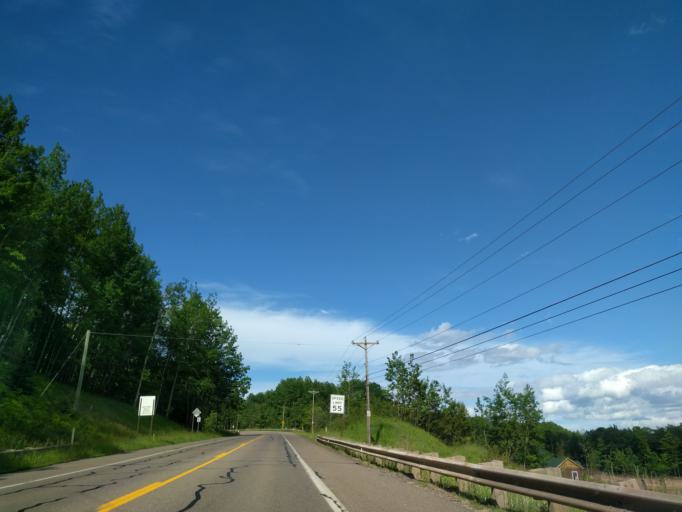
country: US
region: Michigan
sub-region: Marquette County
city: Marquette
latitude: 46.5095
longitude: -87.4177
